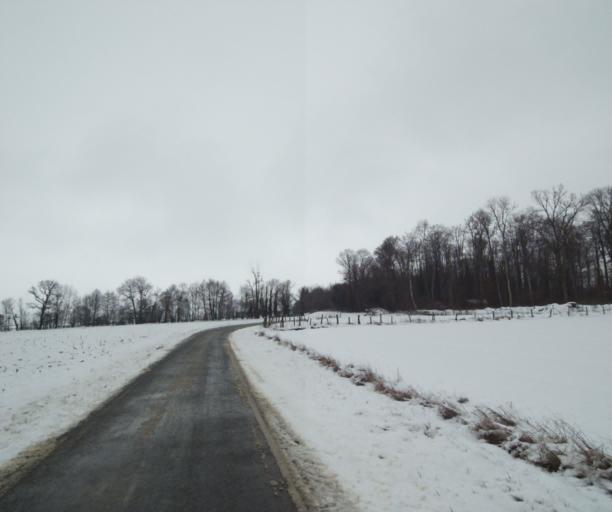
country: FR
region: Champagne-Ardenne
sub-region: Departement de la Haute-Marne
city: Wassy
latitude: 48.4510
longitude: 4.9514
